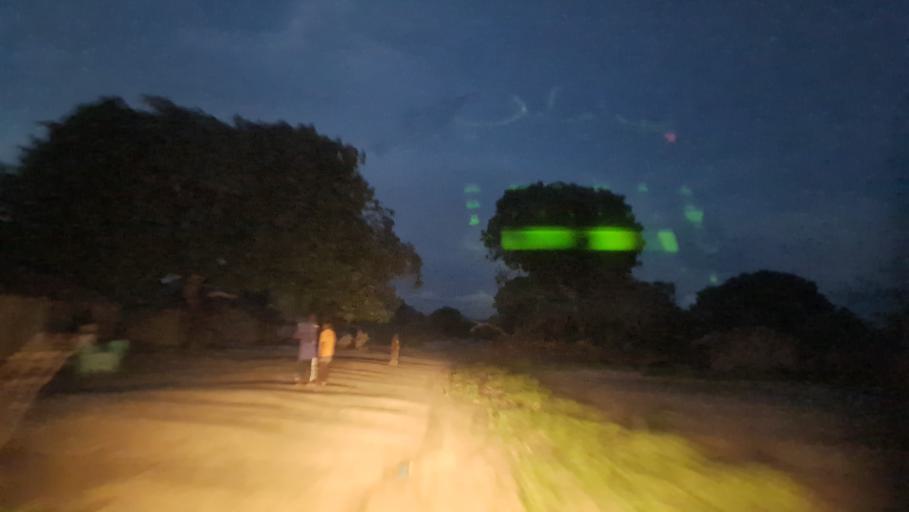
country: MZ
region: Nampula
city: Nampula
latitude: -14.6665
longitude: 39.8366
